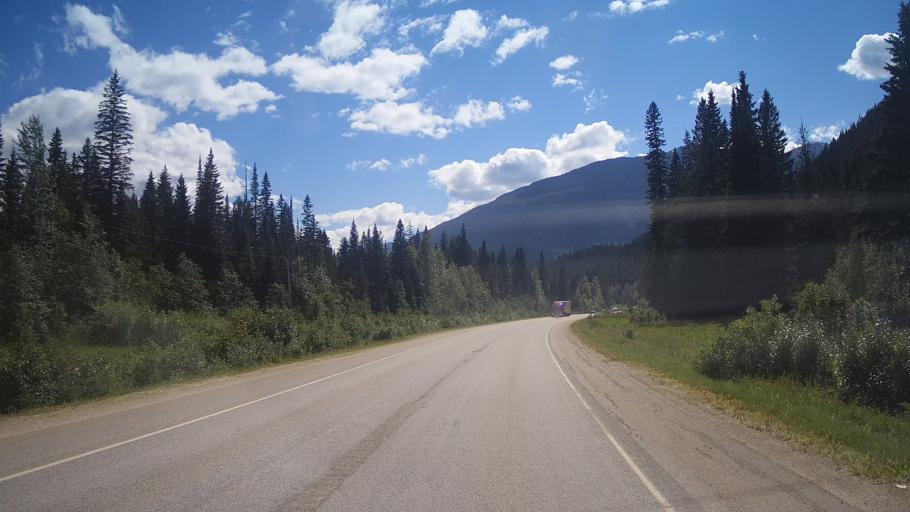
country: CA
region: Alberta
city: Jasper Park Lodge
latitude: 52.5687
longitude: -119.1018
